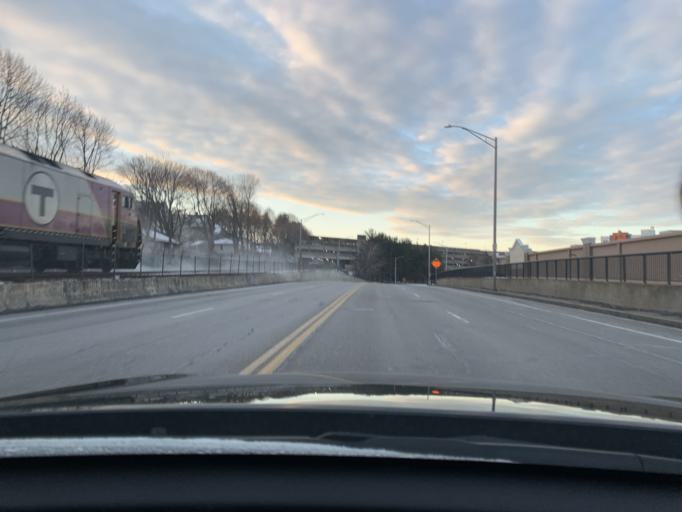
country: US
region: Massachusetts
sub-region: Norfolk County
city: Braintree
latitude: 42.2359
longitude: -71.0066
